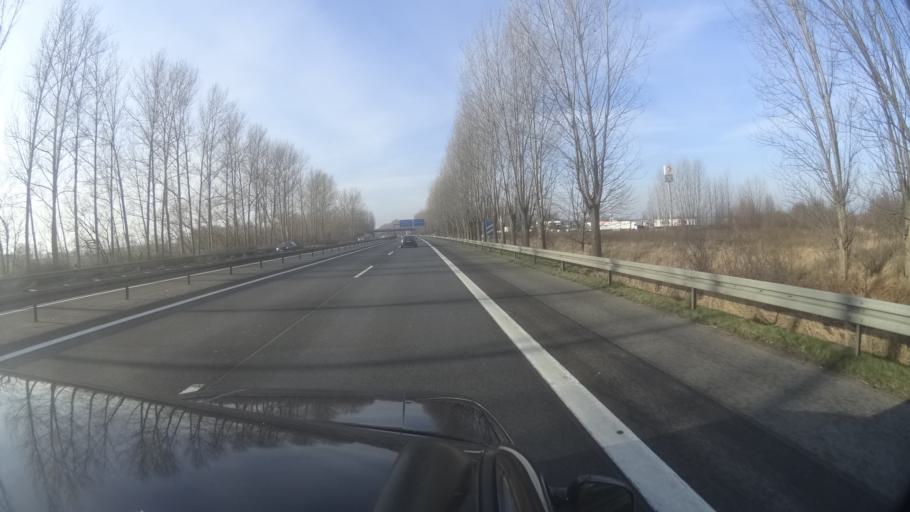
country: DE
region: Brandenburg
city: Velten
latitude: 52.7075
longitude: 13.1112
